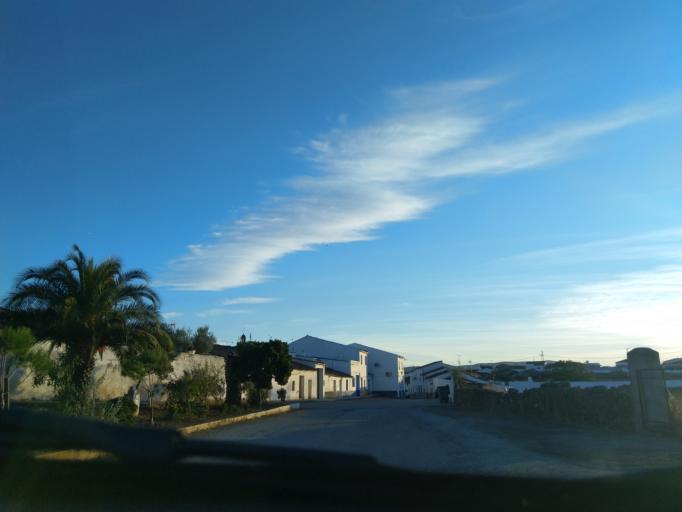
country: ES
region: Extremadura
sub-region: Provincia de Badajoz
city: Valverde de Llerena
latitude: 38.2165
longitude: -5.8215
